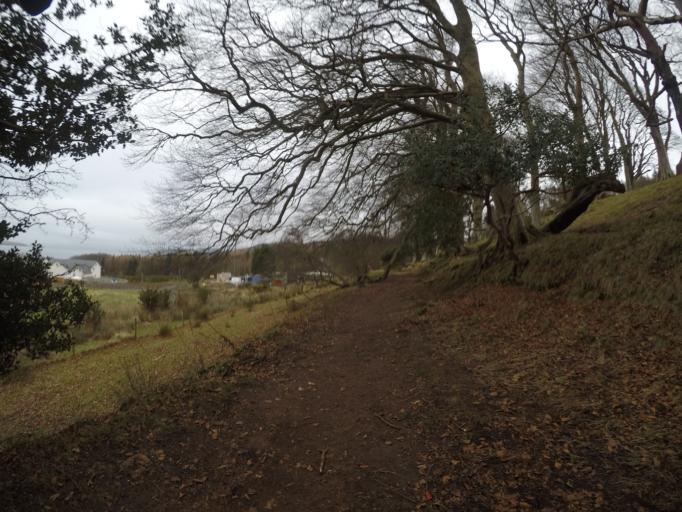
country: GB
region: Scotland
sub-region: North Ayrshire
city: Fairlie
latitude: 55.7604
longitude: -4.8495
